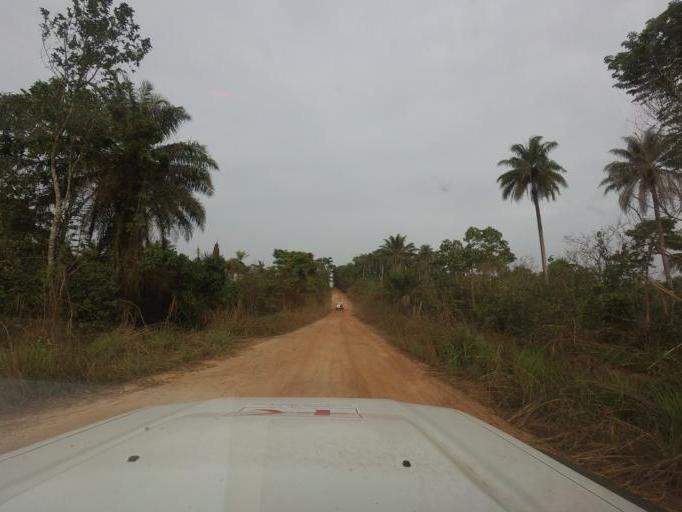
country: LR
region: Lofa
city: Voinjama
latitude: 8.3753
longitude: -9.8638
